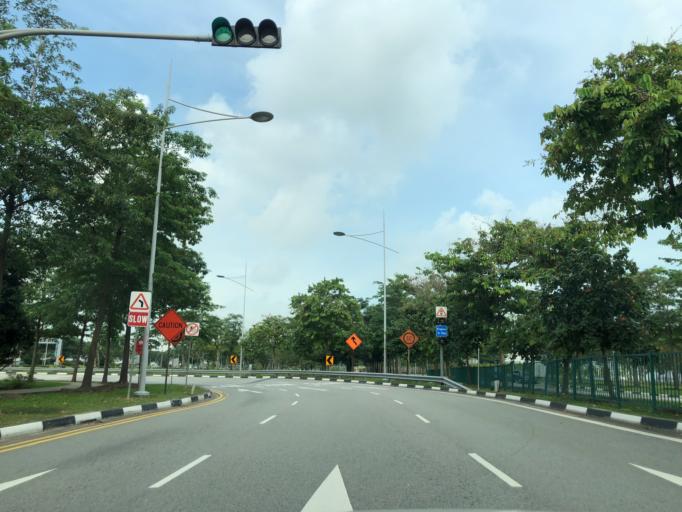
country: SG
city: Singapore
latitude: 1.2717
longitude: 103.8633
